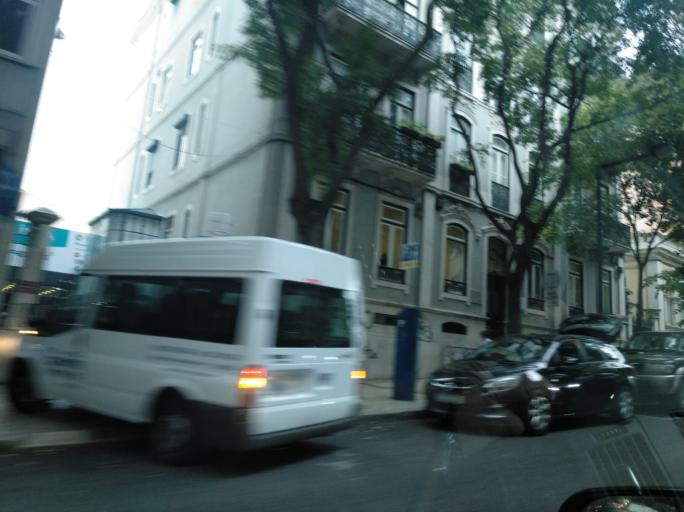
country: PT
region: Lisbon
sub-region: Lisbon
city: Lisbon
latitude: 38.7335
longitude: -9.1413
